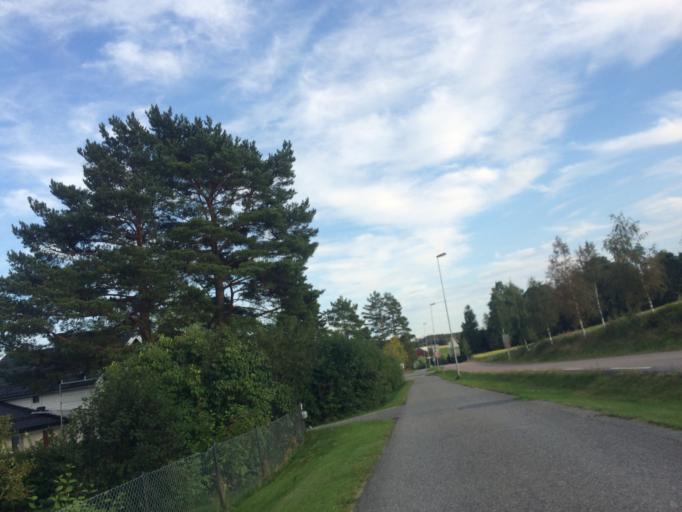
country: NO
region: Akershus
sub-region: Ski
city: Ski
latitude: 59.6765
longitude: 10.8854
